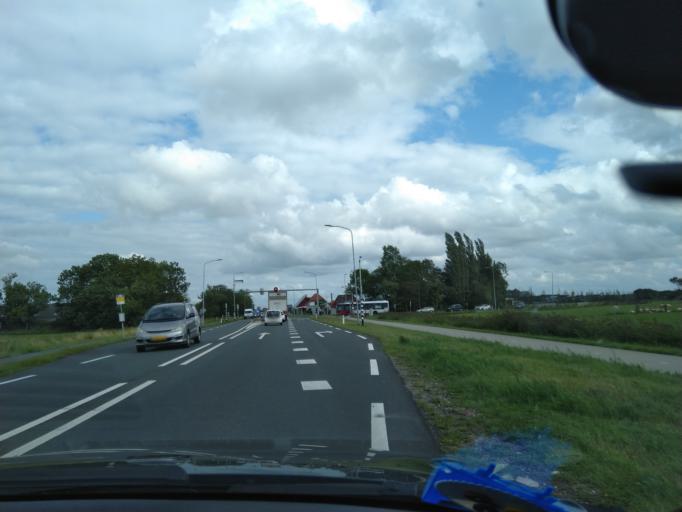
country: NL
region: Groningen
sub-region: Gemeente Zuidhorn
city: Aduard
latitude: 53.2431
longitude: 6.4924
